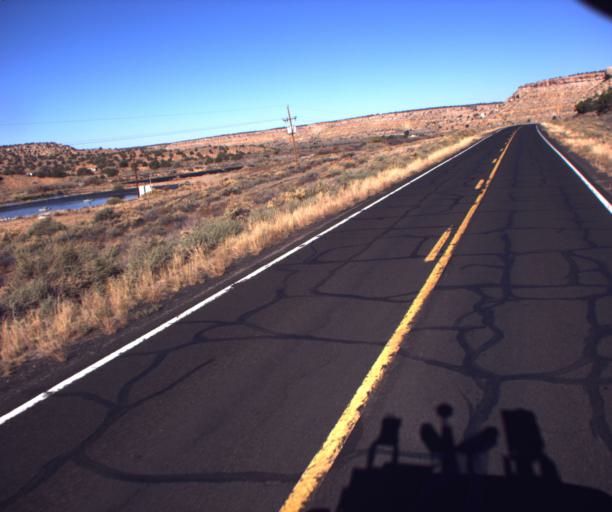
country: US
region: Arizona
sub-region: Navajo County
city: First Mesa
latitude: 35.8321
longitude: -110.2264
